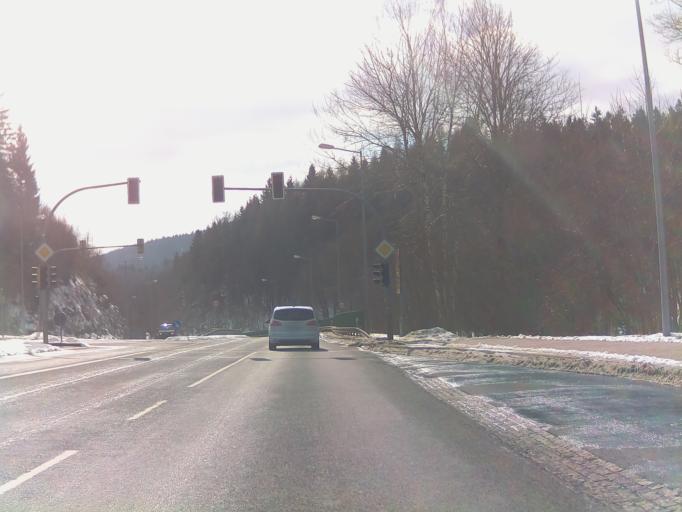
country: DE
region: Thuringia
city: Suhl
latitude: 50.6335
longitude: 10.6977
